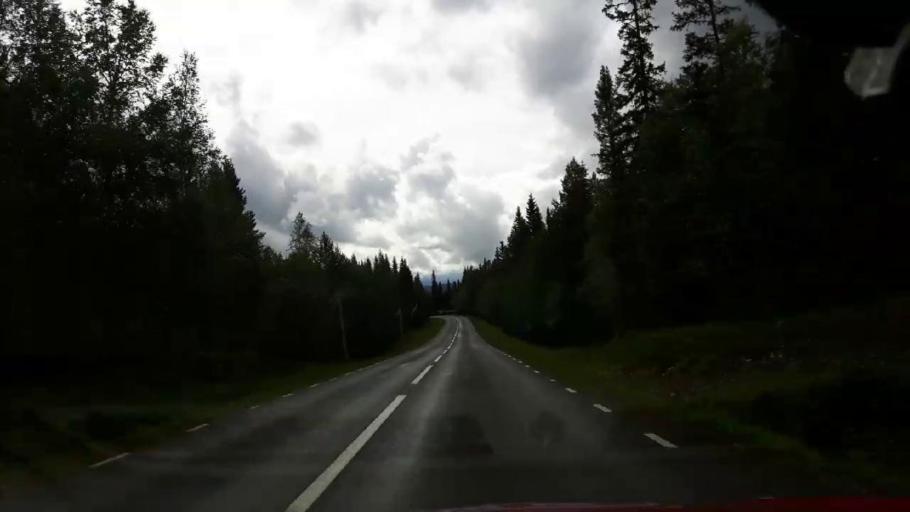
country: NO
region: Nord-Trondelag
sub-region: Lierne
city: Sandvika
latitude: 64.5135
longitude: 14.1571
